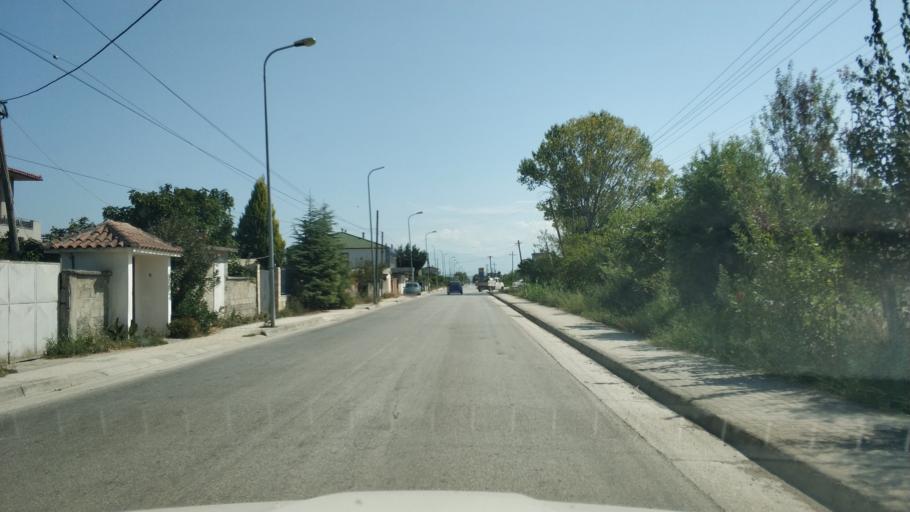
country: AL
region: Fier
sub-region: Rrethi i Lushnjes
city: Krutja e Poshtme
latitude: 40.8922
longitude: 19.6365
